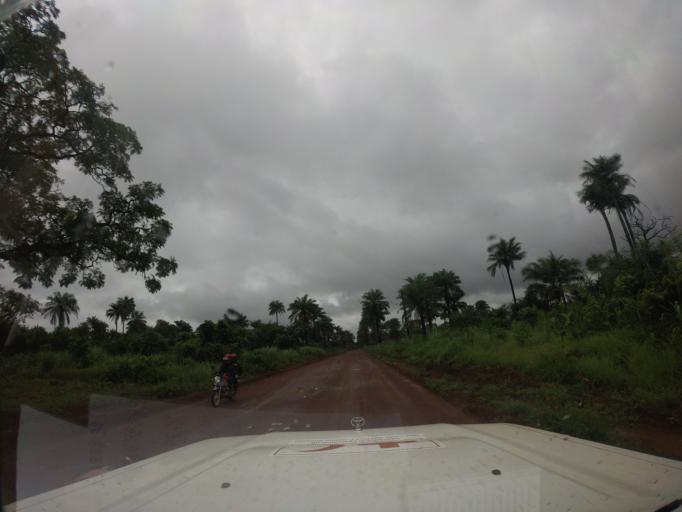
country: SL
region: Northern Province
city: Kambia
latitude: 9.1297
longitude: -12.8931
